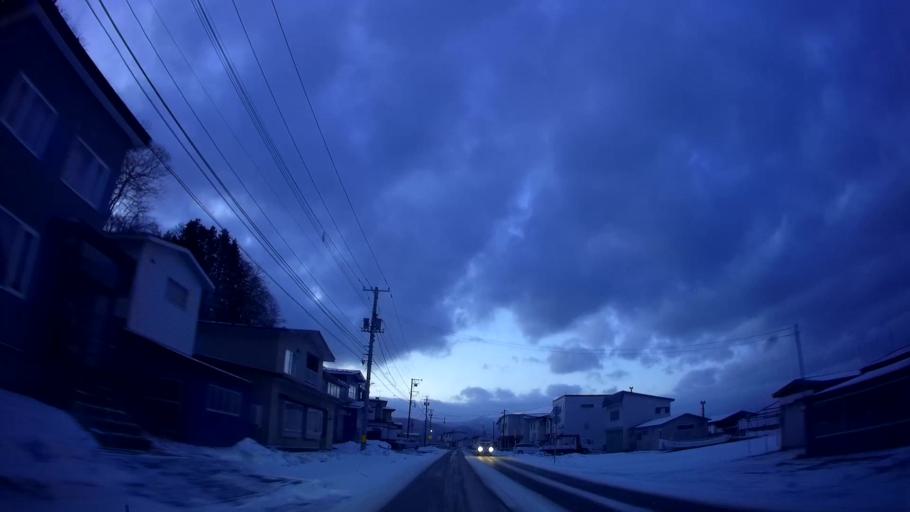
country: JP
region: Hokkaido
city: Hakodate
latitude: 41.8944
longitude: 141.0350
